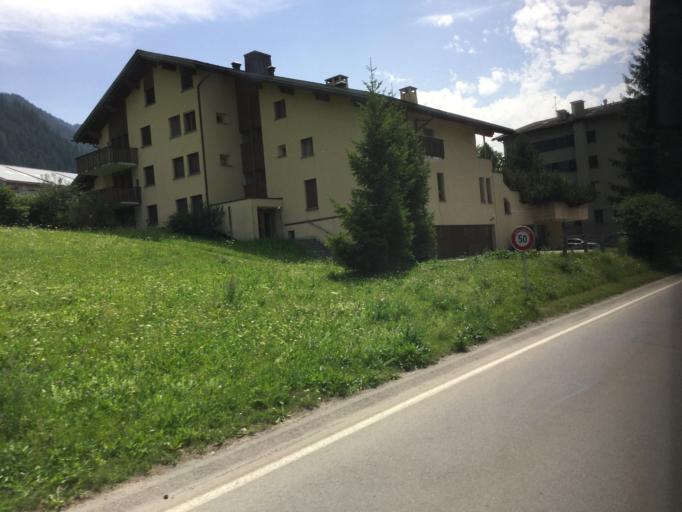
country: CH
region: Grisons
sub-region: Albula District
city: Tiefencastel
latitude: 46.6112
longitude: 9.5918
